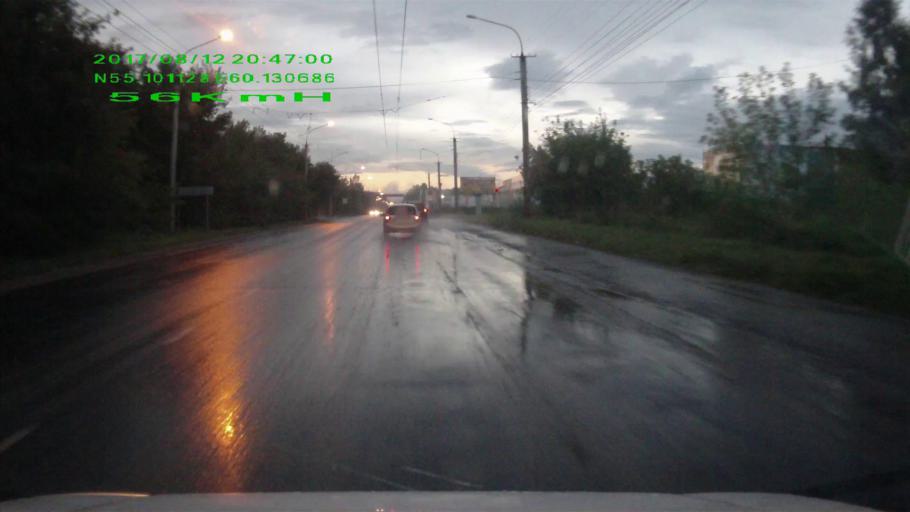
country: RU
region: Chelyabinsk
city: Turgoyak
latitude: 55.1015
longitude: 60.1307
